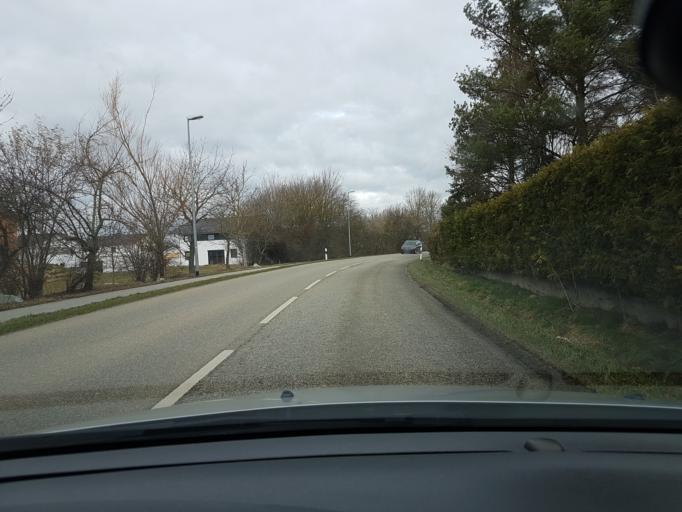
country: DE
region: Bavaria
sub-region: Lower Bavaria
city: Vilsbiburg
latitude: 48.4577
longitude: 12.3485
